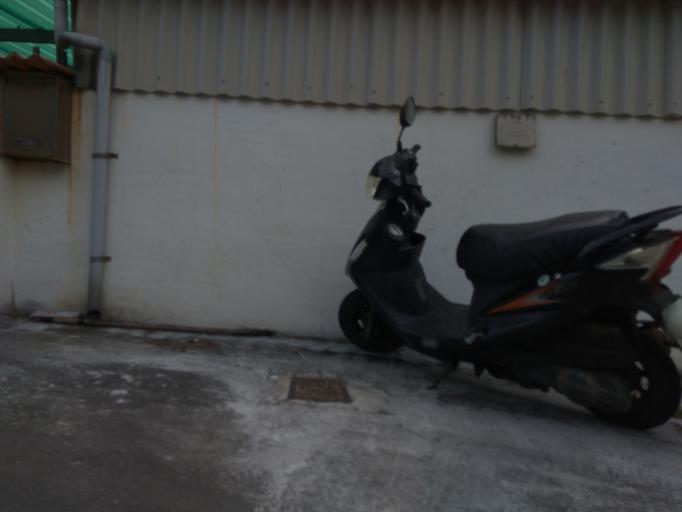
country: TW
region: Taiwan
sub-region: Hsinchu
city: Zhubei
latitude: 24.9754
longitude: 121.0158
